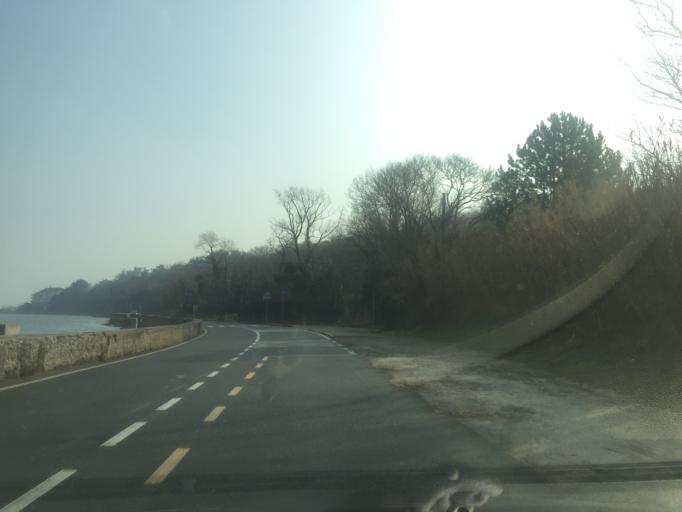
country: IT
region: Friuli Venezia Giulia
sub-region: Provincia di Trieste
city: Muggia
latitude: 45.6089
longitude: 13.7411
